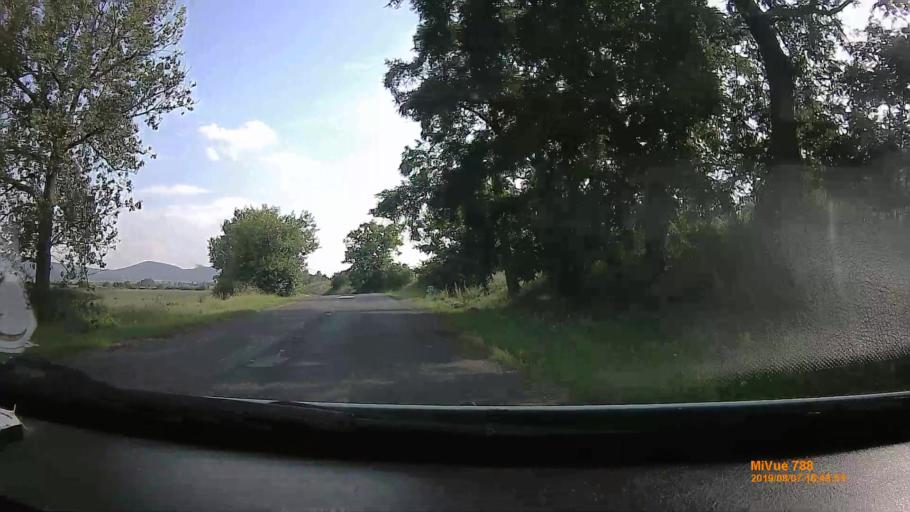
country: HU
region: Borsod-Abauj-Zemplen
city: Abaujszanto
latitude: 48.3268
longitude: 21.2017
